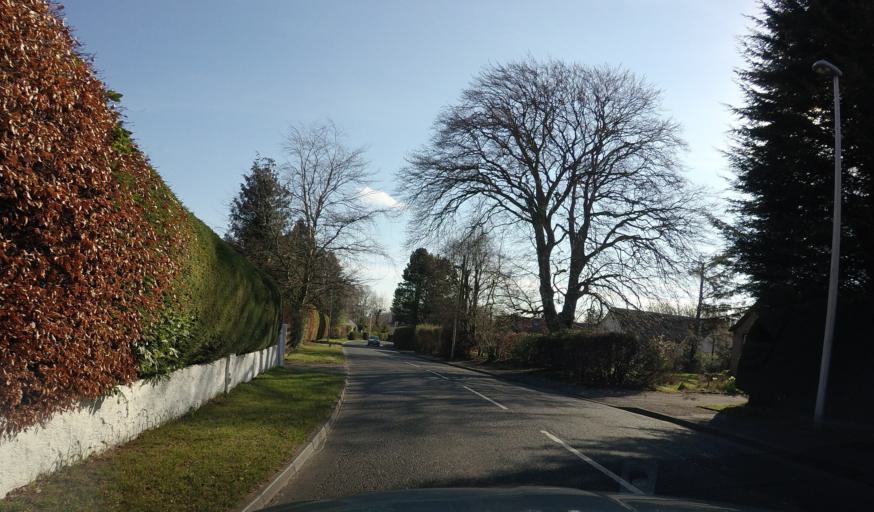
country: GB
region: Scotland
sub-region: Midlothian
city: Penicuik
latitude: 55.8477
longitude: -3.2102
